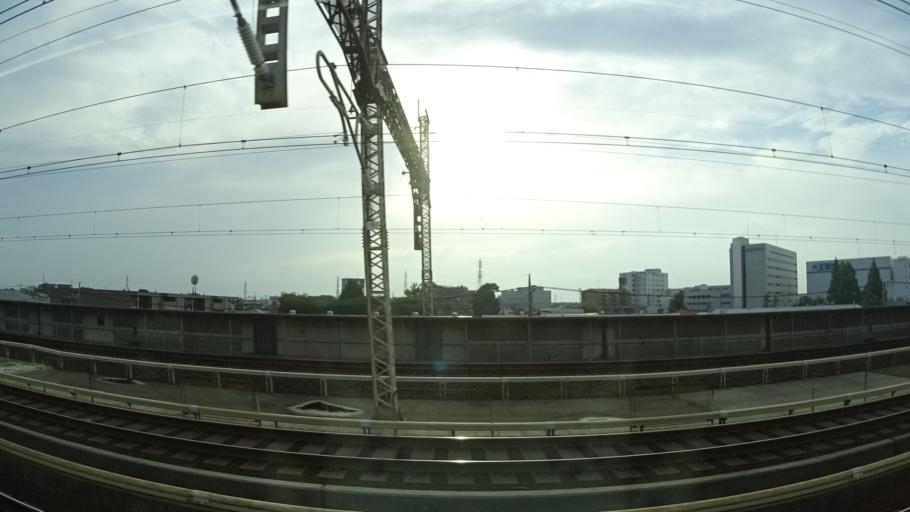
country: JP
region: Saitama
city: Ageoshimo
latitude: 35.9527
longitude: 139.6202
